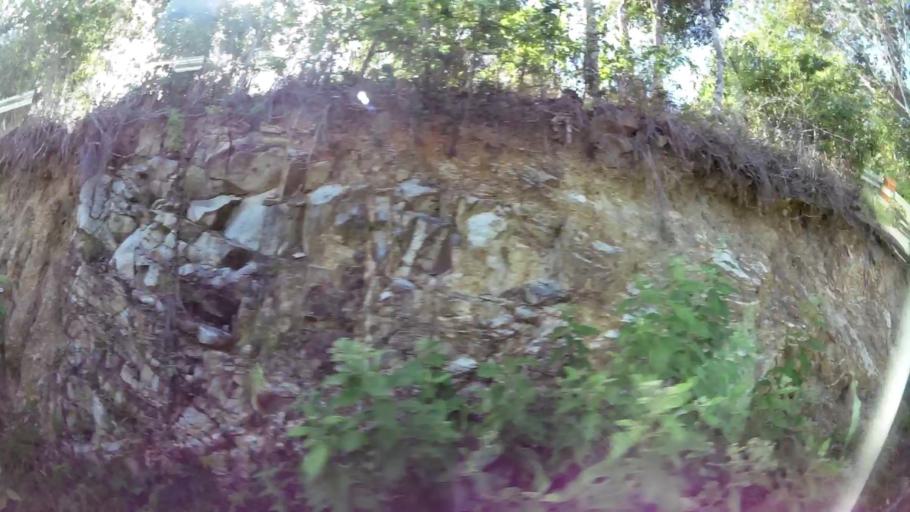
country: VG
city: Tortola
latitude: 18.4882
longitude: -64.3986
